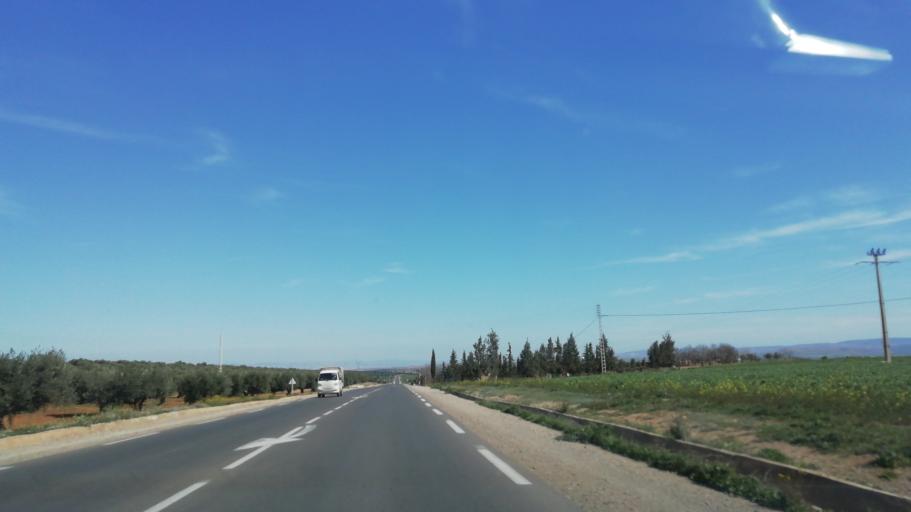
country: DZ
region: Mascara
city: Mascara
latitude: 35.4170
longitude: 0.4039
